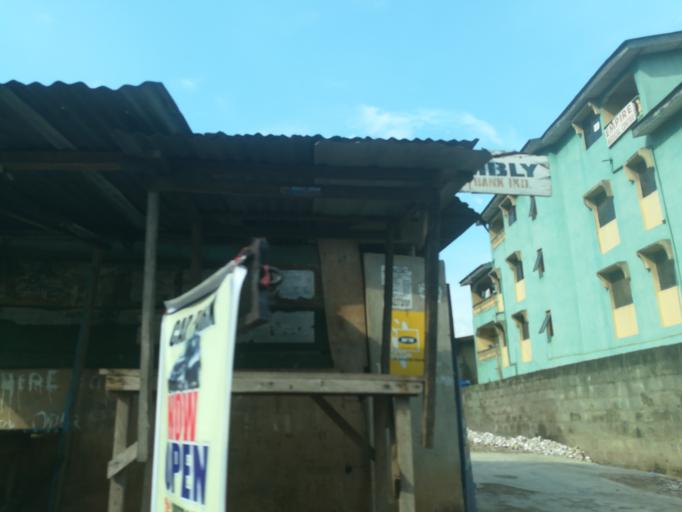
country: NG
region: Lagos
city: Ikorodu
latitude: 6.6219
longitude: 3.5026
